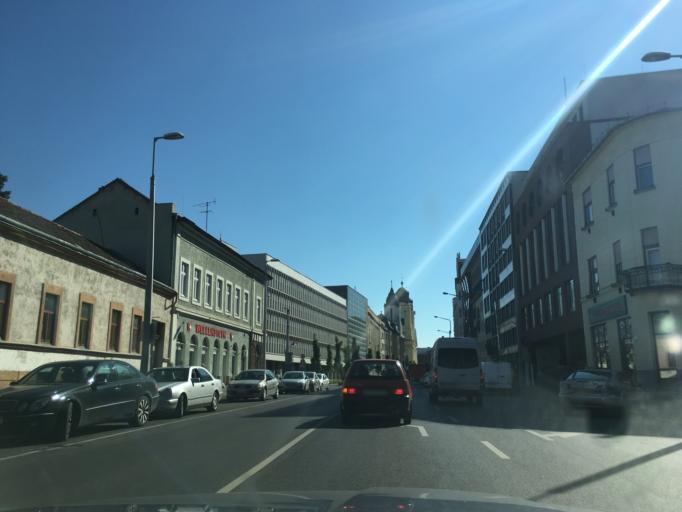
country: HU
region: Hajdu-Bihar
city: Debrecen
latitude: 47.5309
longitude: 21.6203
